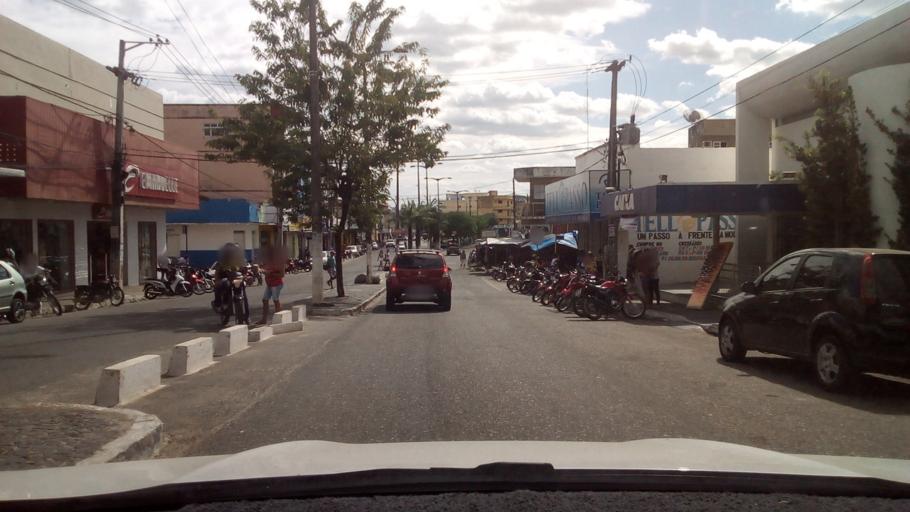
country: BR
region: Paraiba
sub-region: Guarabira
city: Guarabira
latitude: -6.8499
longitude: -35.4909
